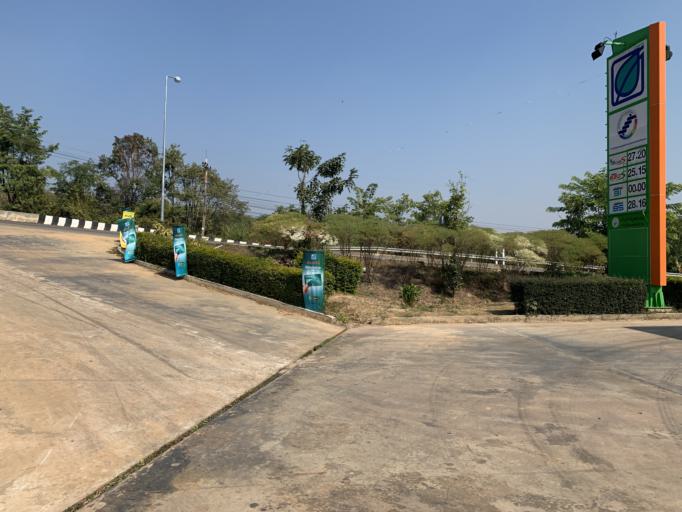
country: TH
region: Phetchabun
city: Nam Nao
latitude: 16.7297
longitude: 101.7476
